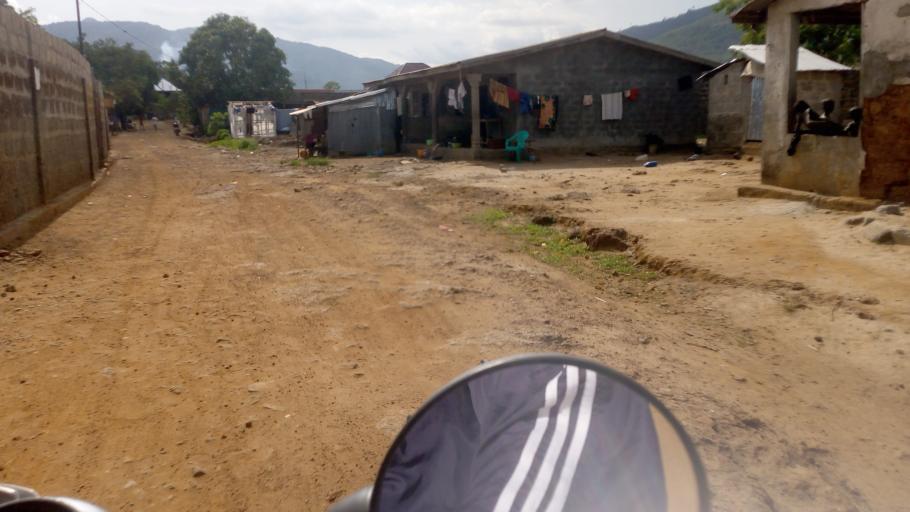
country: SL
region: Western Area
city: Waterloo
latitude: 8.3219
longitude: -13.0812
